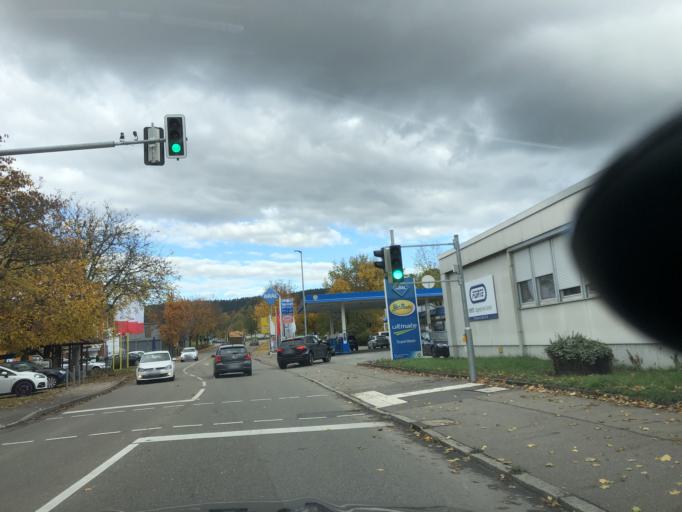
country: DE
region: Baden-Wuerttemberg
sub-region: Regierungsbezirk Stuttgart
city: Winterbach
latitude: 48.8043
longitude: 9.4792
